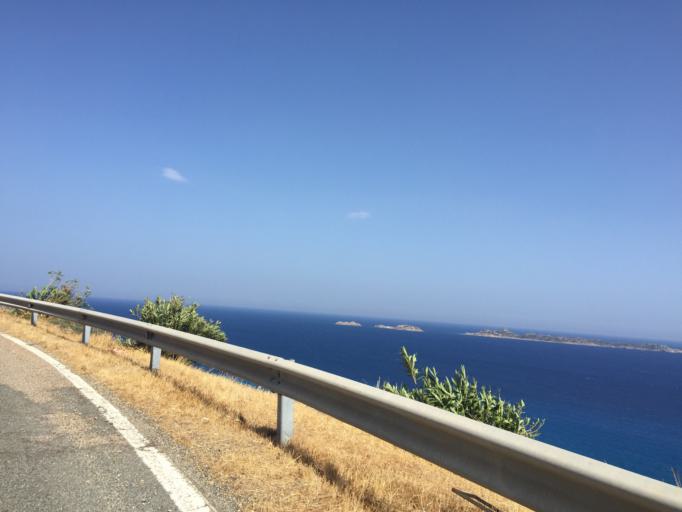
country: IT
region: Sardinia
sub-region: Provincia di Cagliari
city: Villasimius
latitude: 39.1418
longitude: 9.5615
